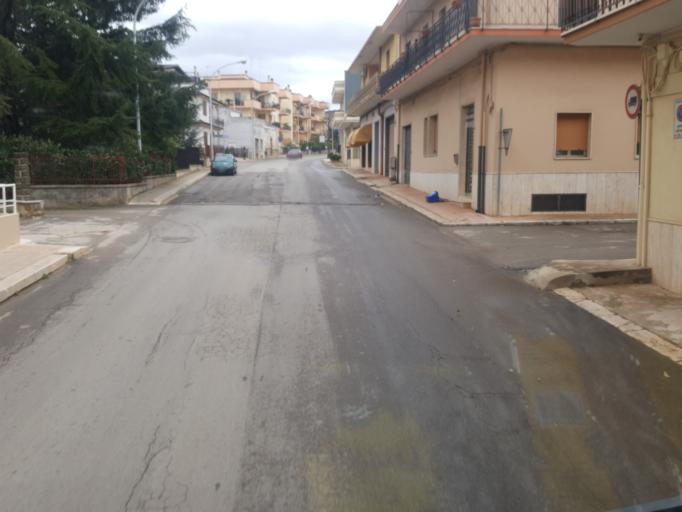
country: IT
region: Apulia
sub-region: Provincia di Bari
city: Turi
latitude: 40.9176
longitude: 17.0261
